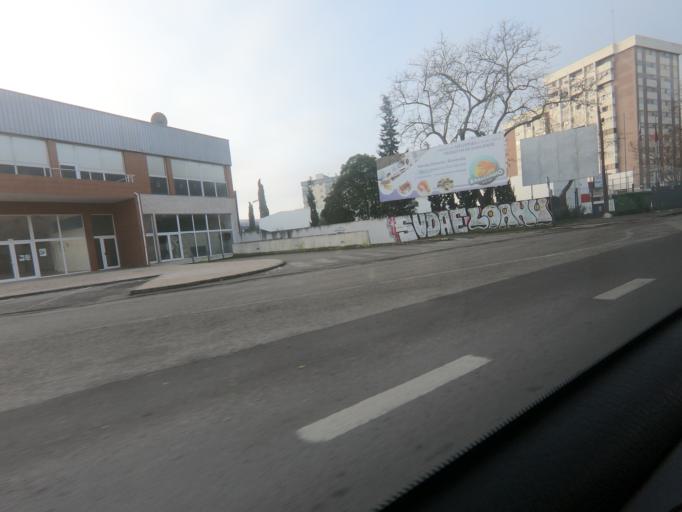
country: PT
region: Setubal
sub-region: Setubal
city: Setubal
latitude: 38.5348
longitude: -8.8655
